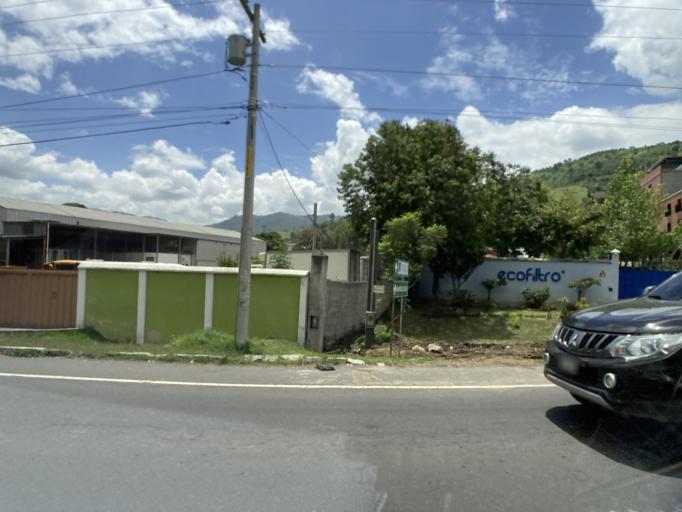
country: GT
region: Sacatepequez
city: San Antonio Aguas Calientes
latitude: 14.5361
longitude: -90.7705
